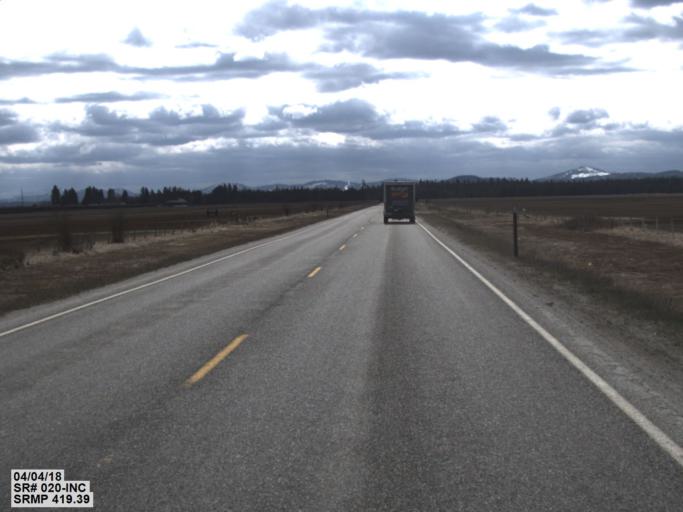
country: US
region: Washington
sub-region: Pend Oreille County
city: Newport
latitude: 48.3324
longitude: -117.3021
